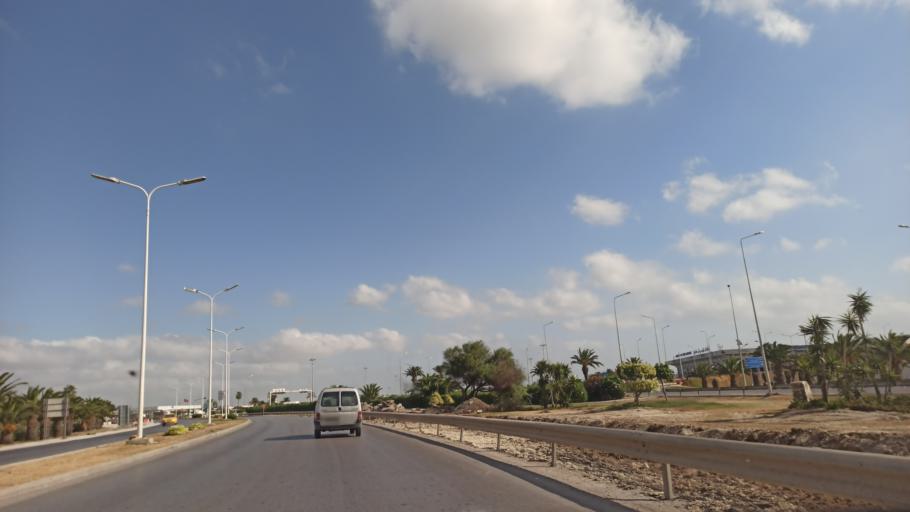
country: TN
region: Ariana
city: Ariana
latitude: 36.8443
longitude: 10.2152
